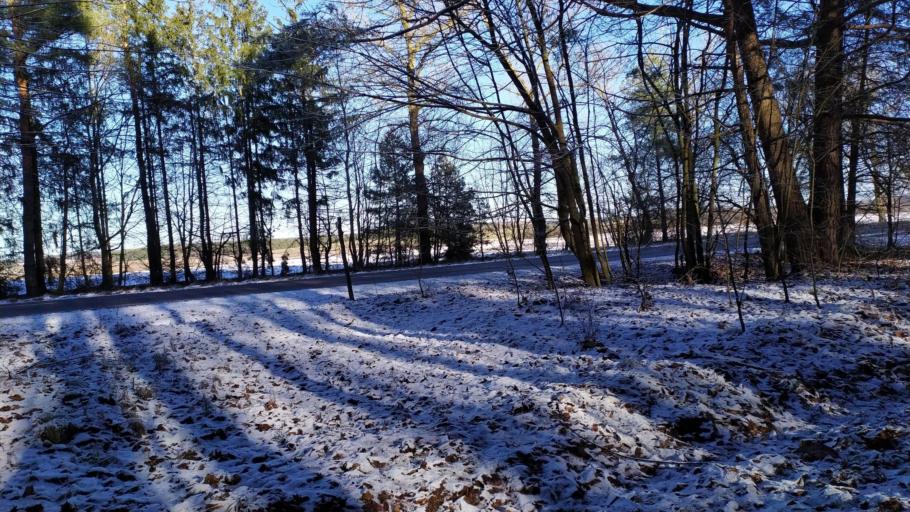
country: BY
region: Brest
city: Kamyanyets
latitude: 52.3763
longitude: 23.8734
